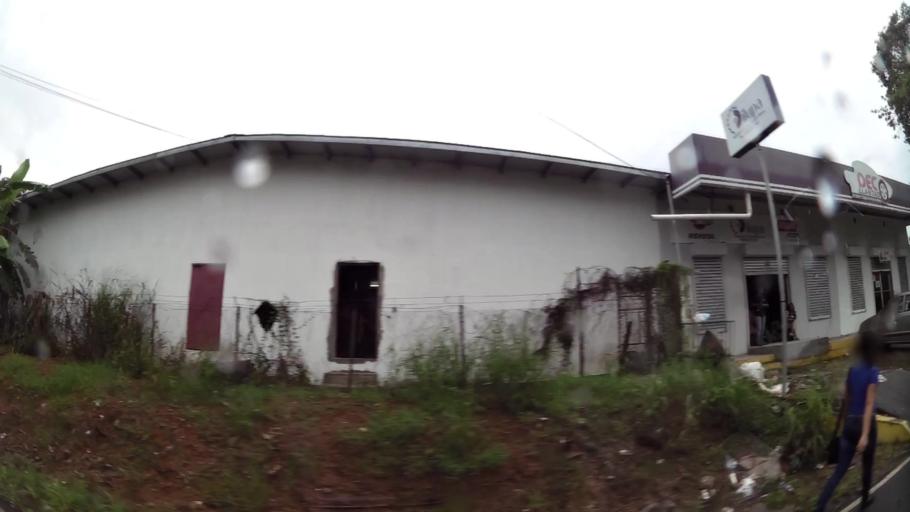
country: PA
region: Veraguas
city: Santiago de Veraguas
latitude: 8.1001
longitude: -80.9707
